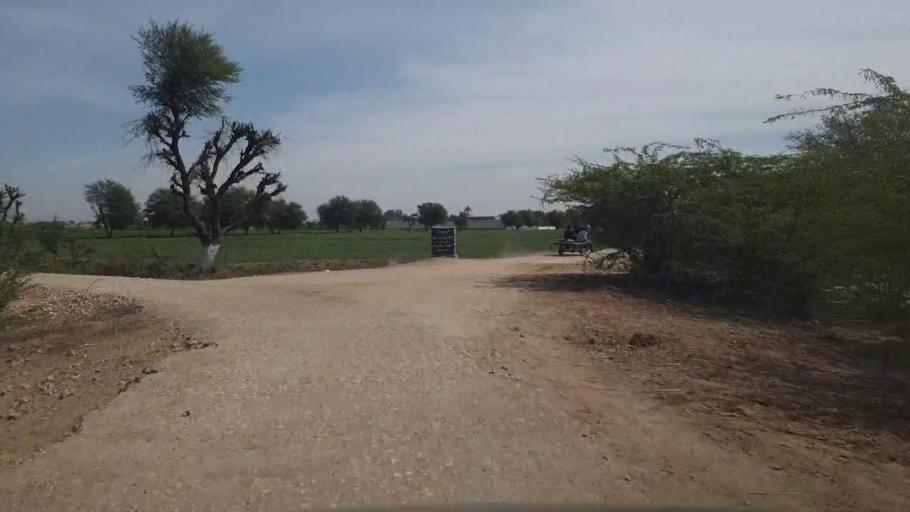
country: PK
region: Sindh
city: Kunri
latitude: 25.2853
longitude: 69.5940
